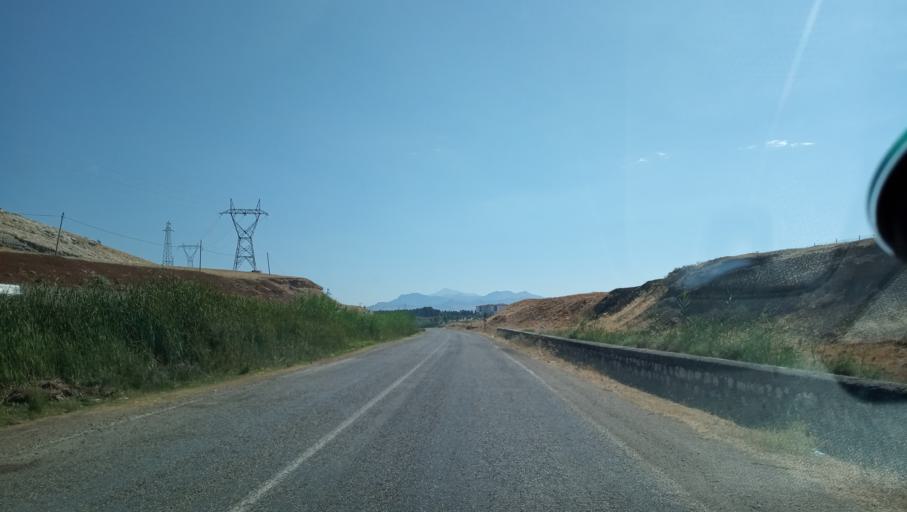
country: TR
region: Diyarbakir
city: Malabadi
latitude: 38.1327
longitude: 41.1863
